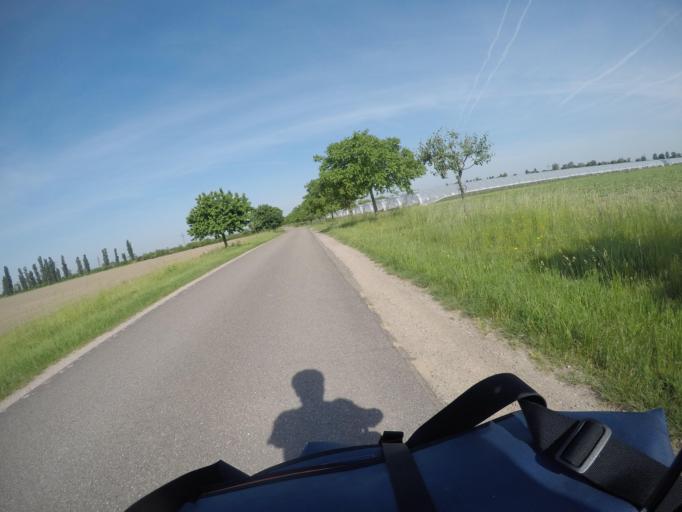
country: DE
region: Baden-Wuerttemberg
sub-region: Karlsruhe Region
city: Rheinstetten
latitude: 48.9329
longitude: 8.3025
